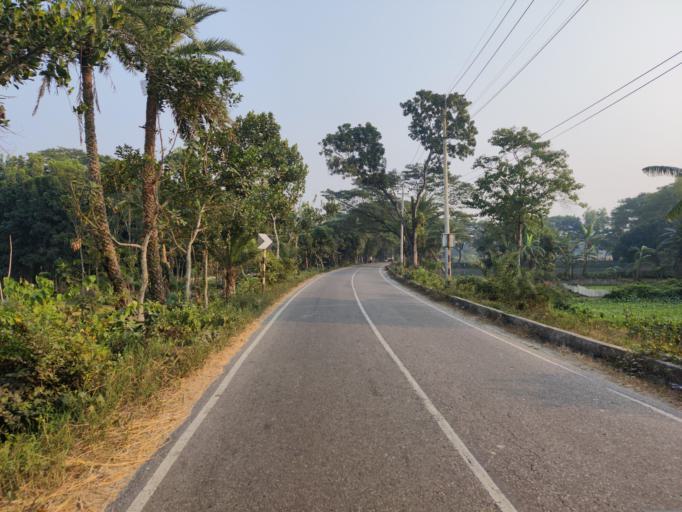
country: BD
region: Dhaka
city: Narsingdi
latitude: 24.0933
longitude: 90.7234
